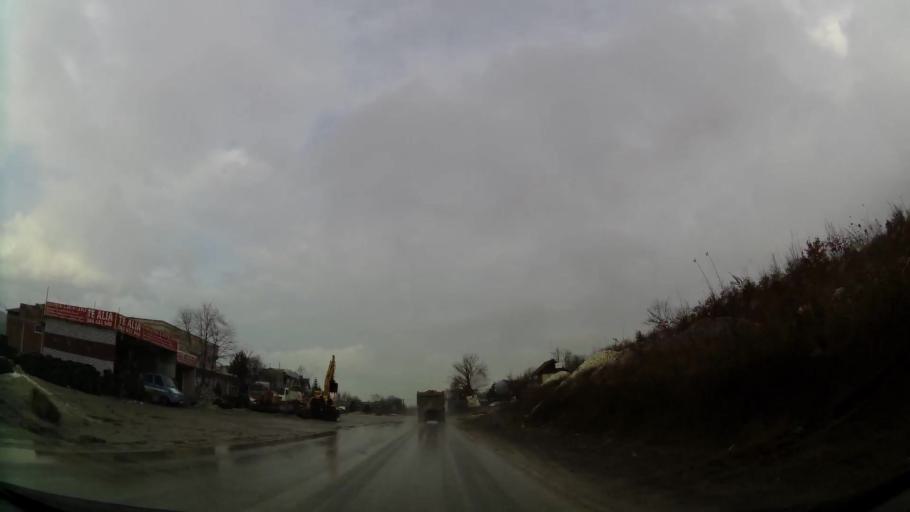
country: XK
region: Ferizaj
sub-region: Komuna e Kacanikut
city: Kacanik
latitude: 42.2484
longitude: 21.2385
